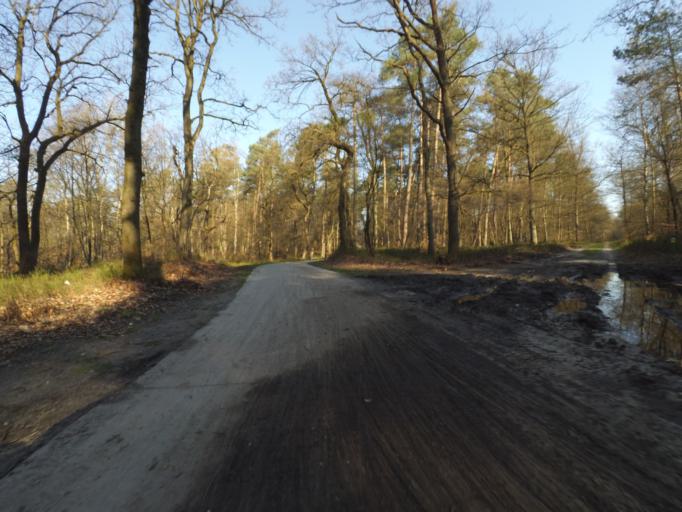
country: NL
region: Gelderland
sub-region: Gemeente Ede
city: Otterlo
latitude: 52.1062
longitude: 5.8726
